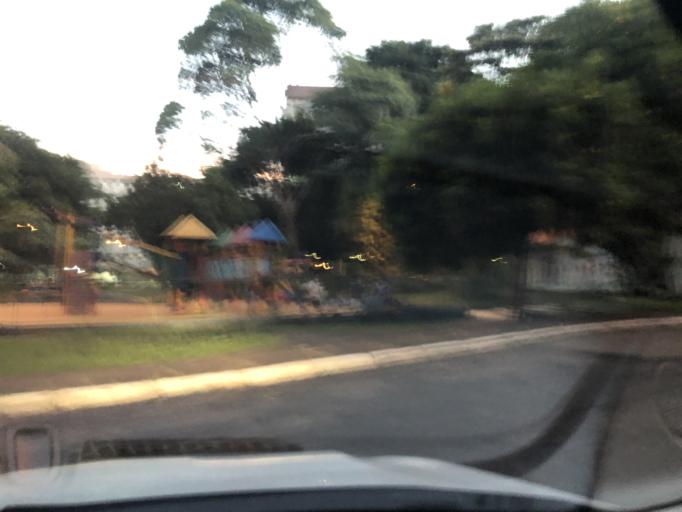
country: BR
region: Federal District
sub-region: Brasilia
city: Brasilia
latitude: -15.8084
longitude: -47.8983
